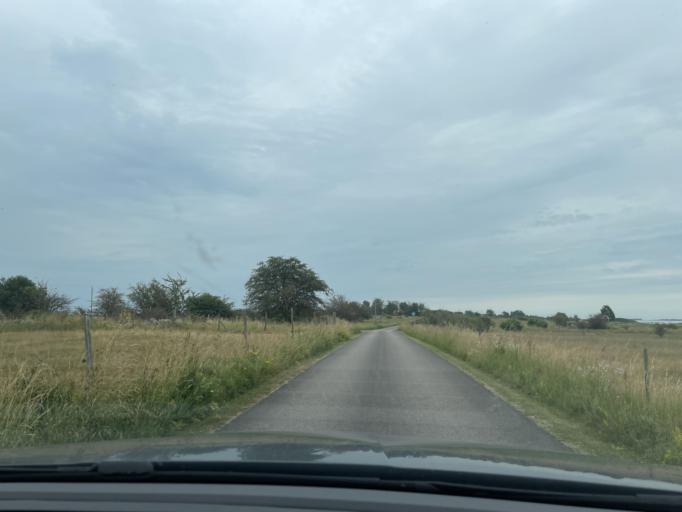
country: SE
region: Skane
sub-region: Bromolla Kommun
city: Bromoella
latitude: 56.0033
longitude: 14.4410
